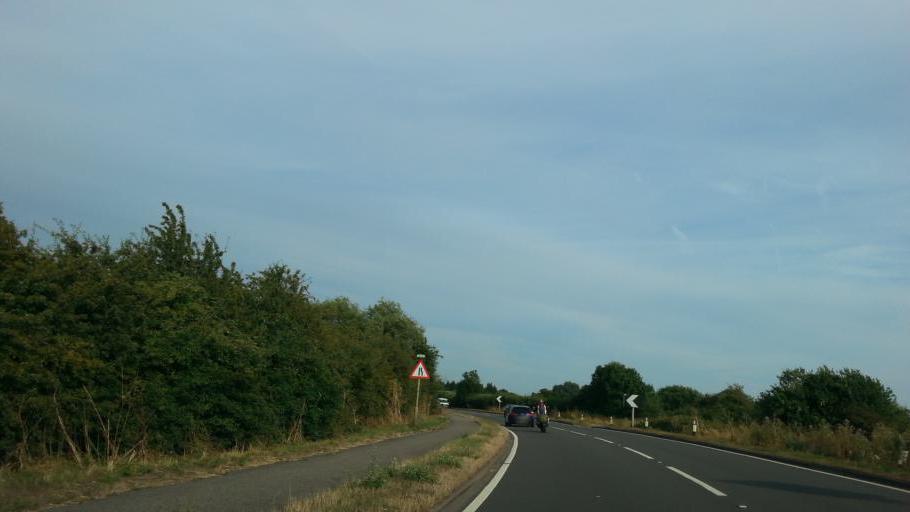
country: GB
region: England
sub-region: Nottinghamshire
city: Newark on Trent
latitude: 53.0838
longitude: -0.8318
